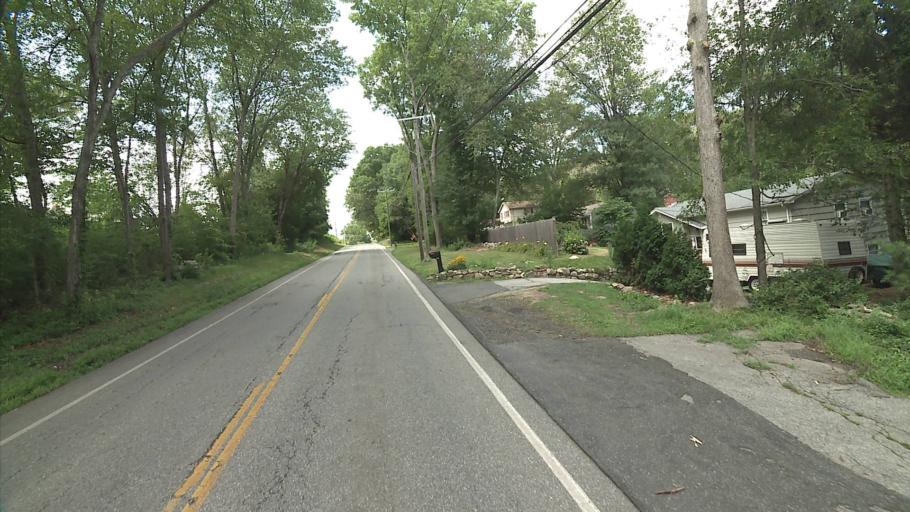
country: US
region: Connecticut
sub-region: New London County
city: Niantic
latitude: 41.3793
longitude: -72.2156
